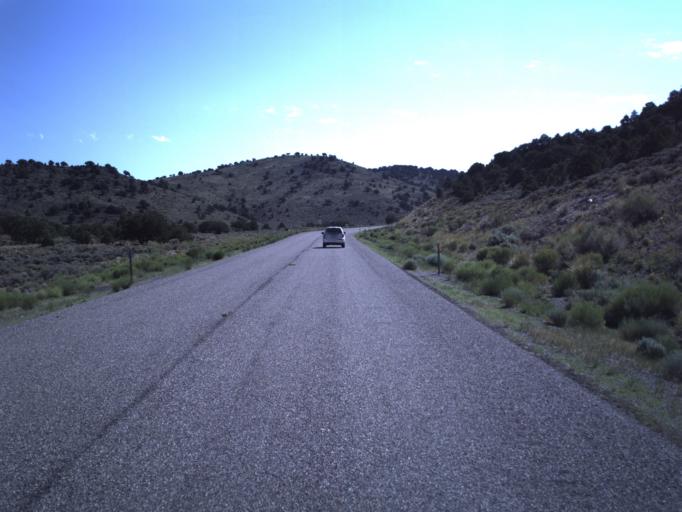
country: US
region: Utah
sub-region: Wayne County
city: Loa
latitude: 38.4777
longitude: -111.5677
